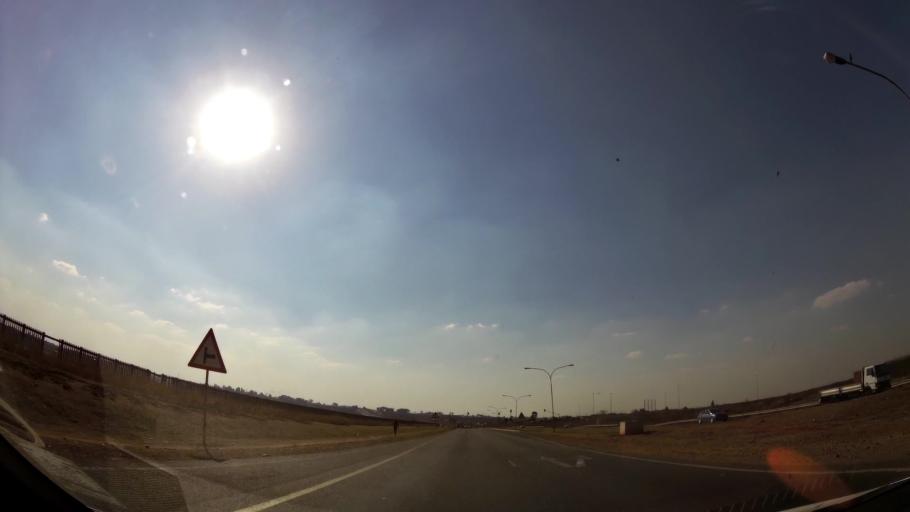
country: ZA
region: Gauteng
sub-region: Ekurhuleni Metropolitan Municipality
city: Benoni
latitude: -26.2354
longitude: 28.3219
